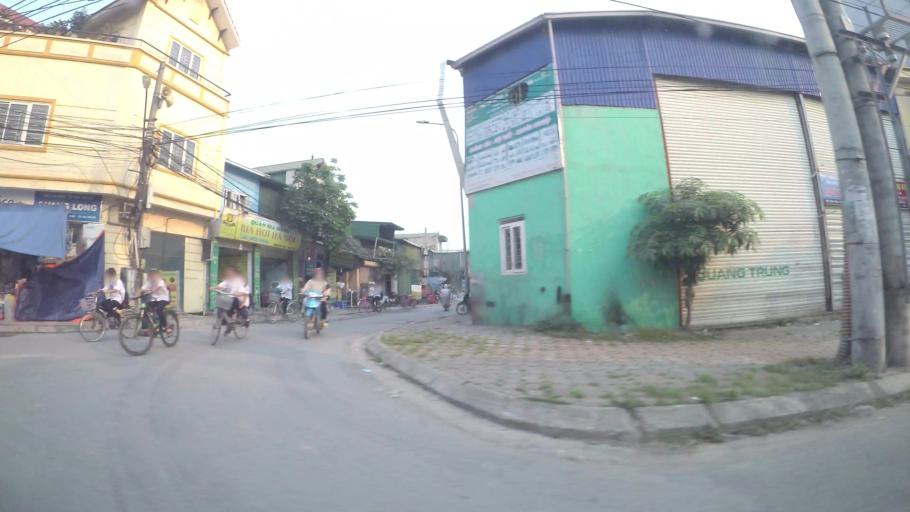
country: VN
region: Ha Noi
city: Van Dien
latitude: 20.9237
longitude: 105.8472
